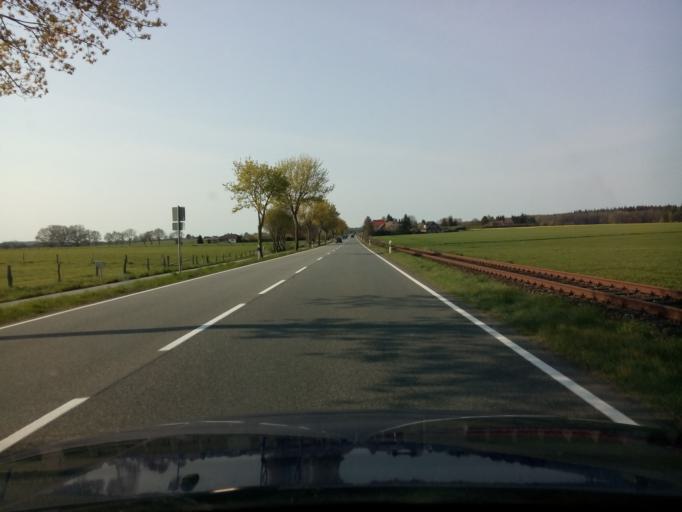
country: DE
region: Lower Saxony
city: Syke
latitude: 52.8913
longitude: 8.8482
